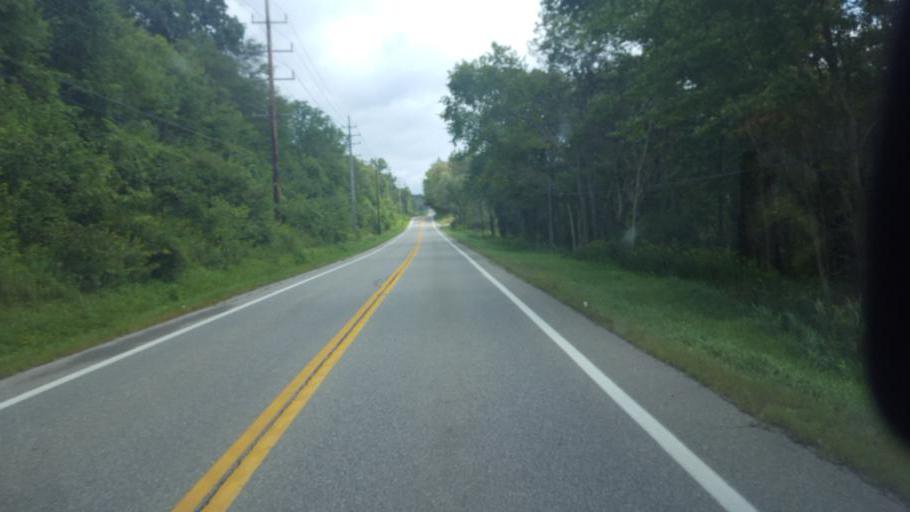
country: US
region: Ohio
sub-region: Geauga County
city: Burton
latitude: 41.5320
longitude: -81.1592
